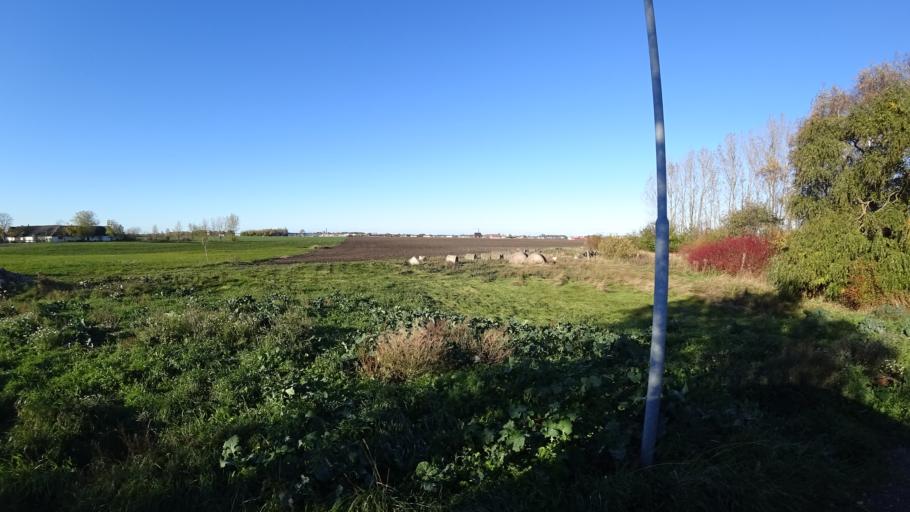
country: SE
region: Skane
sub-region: Staffanstorps Kommun
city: Staffanstorp
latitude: 55.6479
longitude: 13.2505
